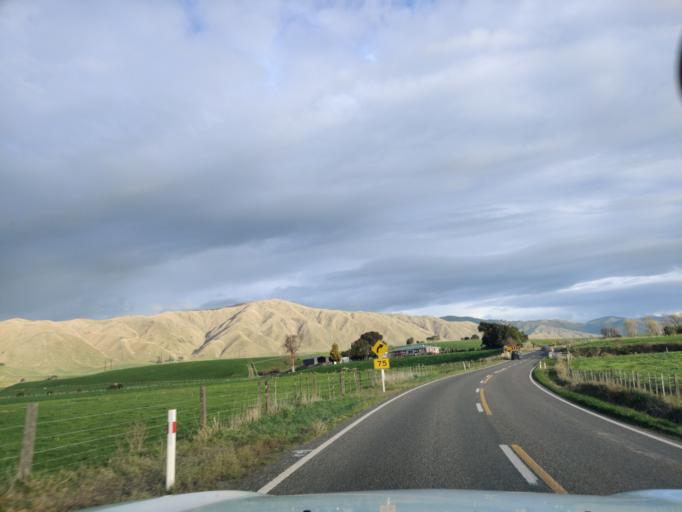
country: NZ
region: Manawatu-Wanganui
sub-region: Palmerston North City
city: Palmerston North
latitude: -40.4953
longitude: 175.4937
